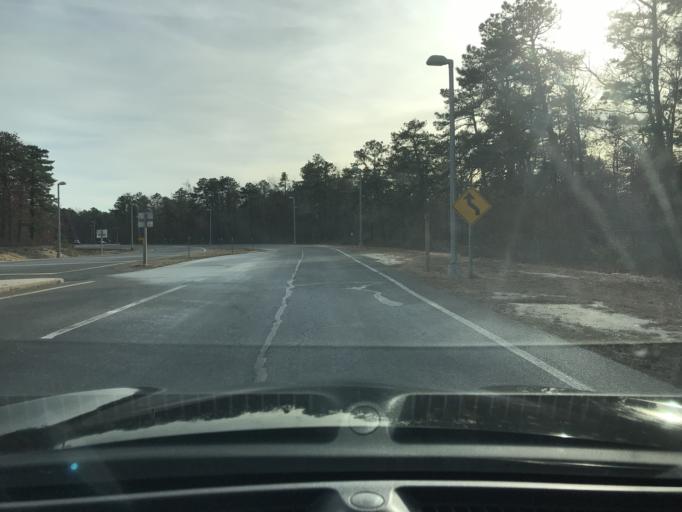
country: US
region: New Jersey
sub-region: Ocean County
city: Waretown
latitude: 39.7950
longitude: -74.2394
